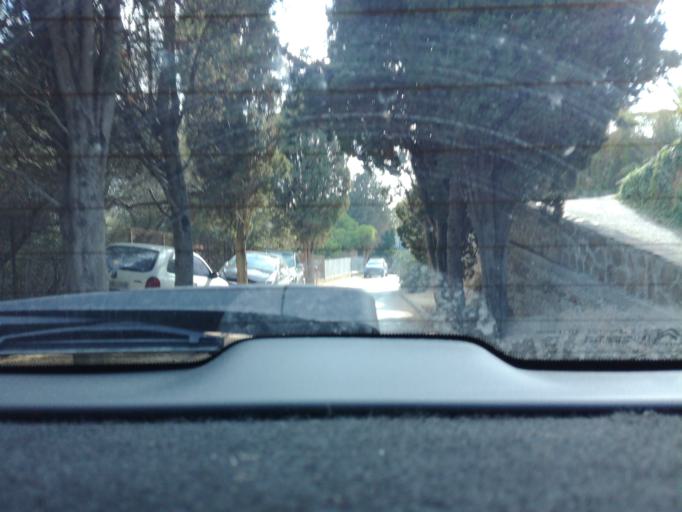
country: FR
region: Provence-Alpes-Cote d'Azur
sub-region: Departement du Var
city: Hyeres
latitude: 43.0378
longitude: 6.1316
